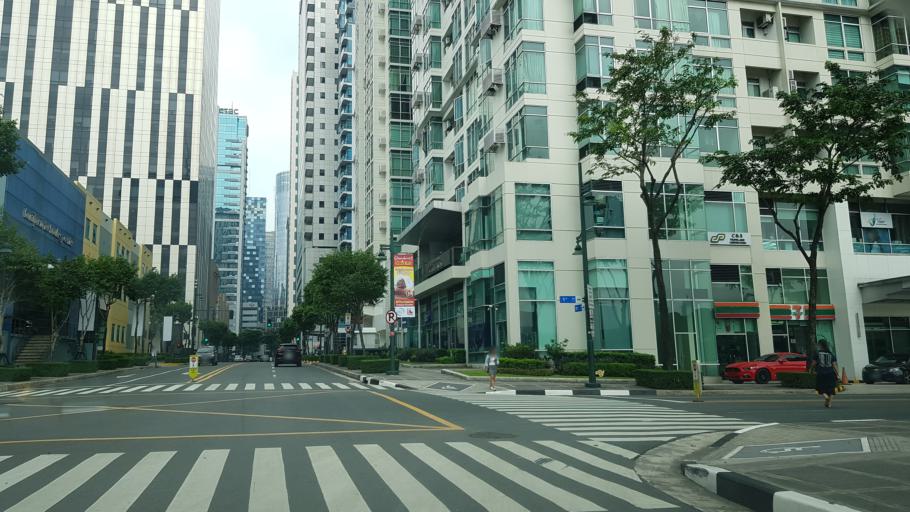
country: PH
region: Metro Manila
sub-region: Makati City
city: Makati City
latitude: 14.5547
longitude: 121.0438
